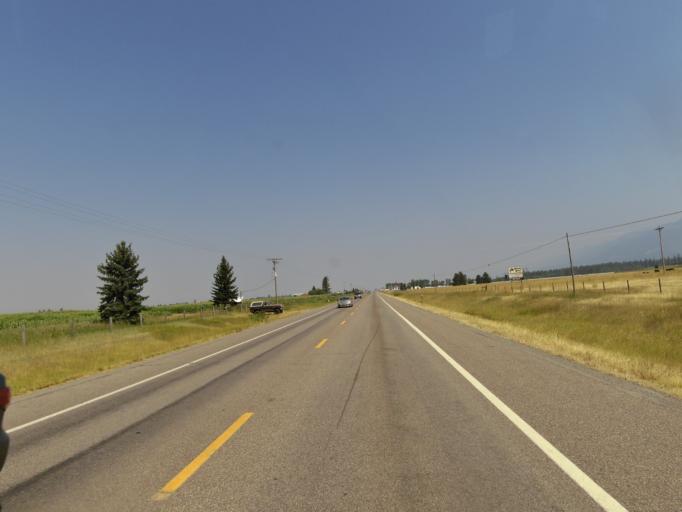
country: US
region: Montana
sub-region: Lake County
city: Ronan
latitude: 47.4960
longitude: -114.0969
